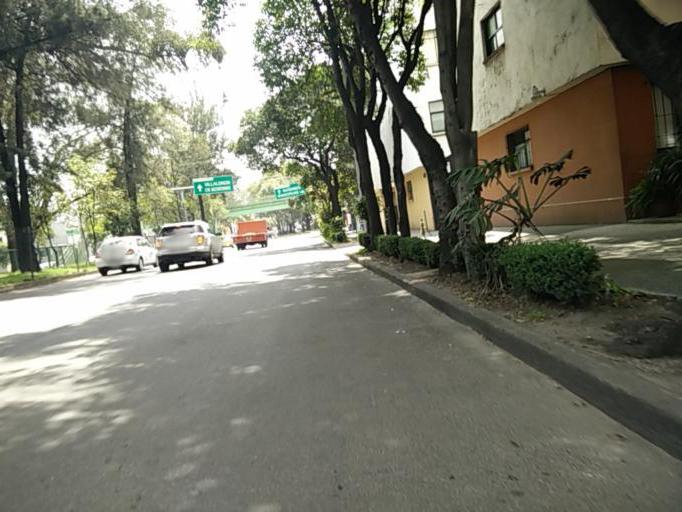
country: MX
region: Mexico City
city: Miguel Hidalgo
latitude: 19.4345
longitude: -99.1766
